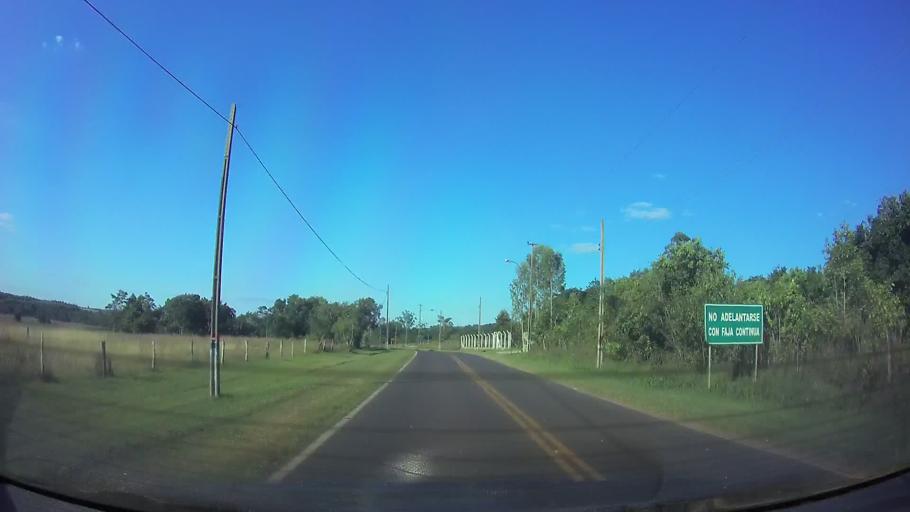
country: PY
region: Cordillera
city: Atyra
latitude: -25.3071
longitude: -57.1878
